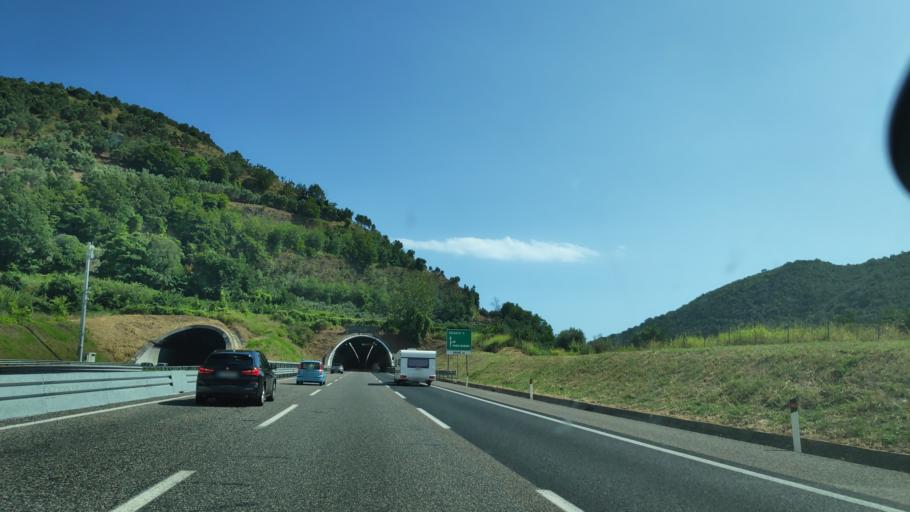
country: IT
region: Campania
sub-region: Provincia di Salerno
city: Pezzano-Filetta
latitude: 40.6788
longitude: 14.8572
